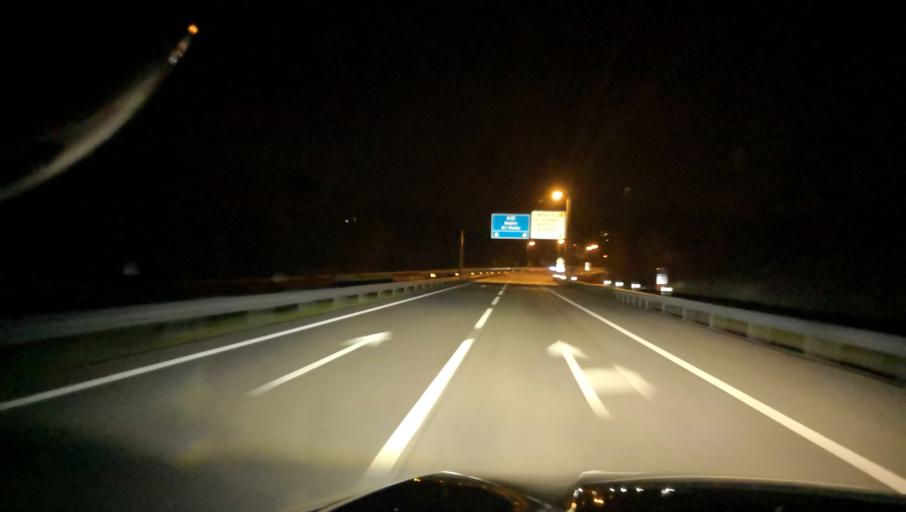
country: PT
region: Viseu
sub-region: Oliveira de Frades
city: Oliveira de Frades
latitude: 40.6828
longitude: -8.1921
